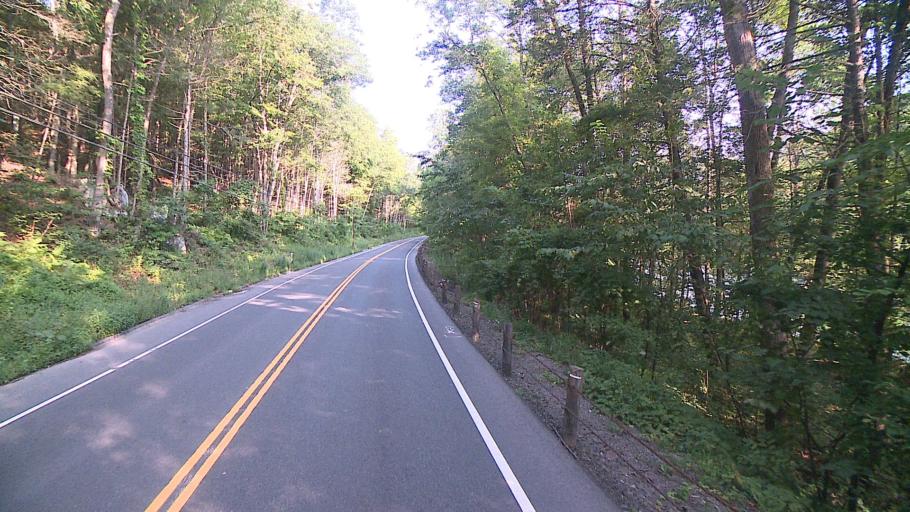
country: US
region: Connecticut
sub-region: Fairfield County
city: Sherman
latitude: 41.6182
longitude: -73.4602
